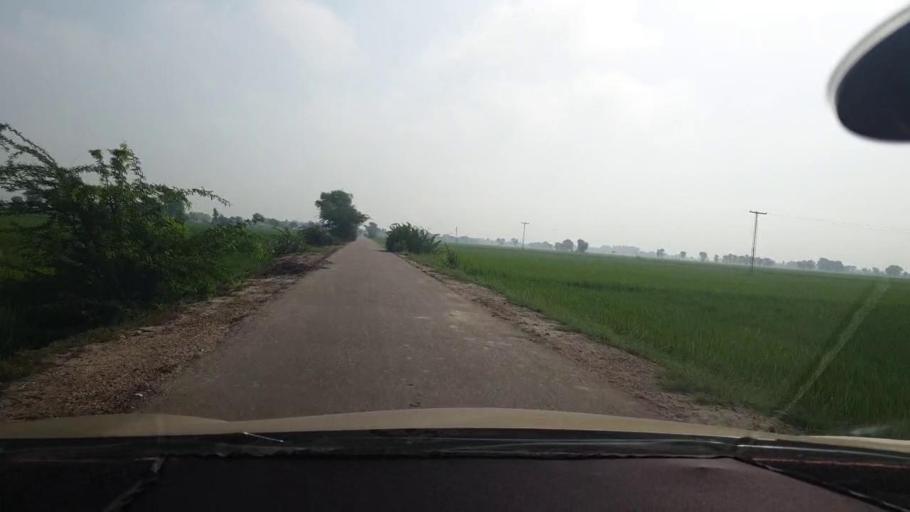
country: PK
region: Sindh
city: Goth Garelo
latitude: 27.4812
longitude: 68.0183
